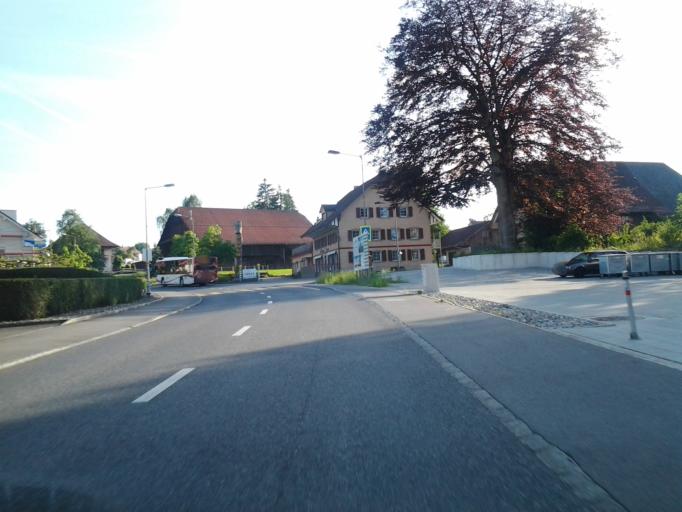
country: CH
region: Lucerne
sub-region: Willisau District
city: Pfaffnau
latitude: 47.2266
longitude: 7.8956
